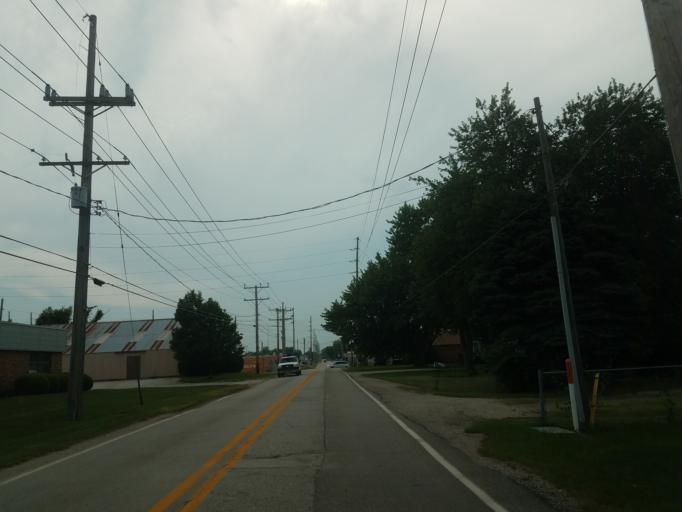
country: US
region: Illinois
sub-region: McLean County
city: Bloomington
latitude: 40.4635
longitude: -88.9834
